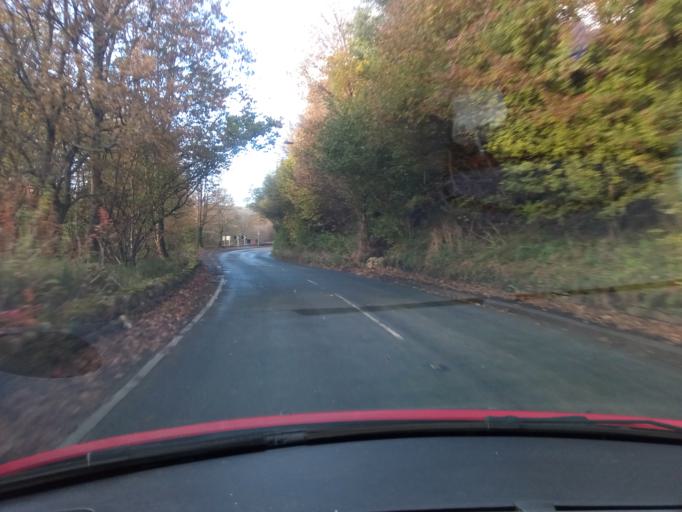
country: GB
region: England
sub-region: County Durham
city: Holwick
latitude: 54.7556
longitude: -2.2248
